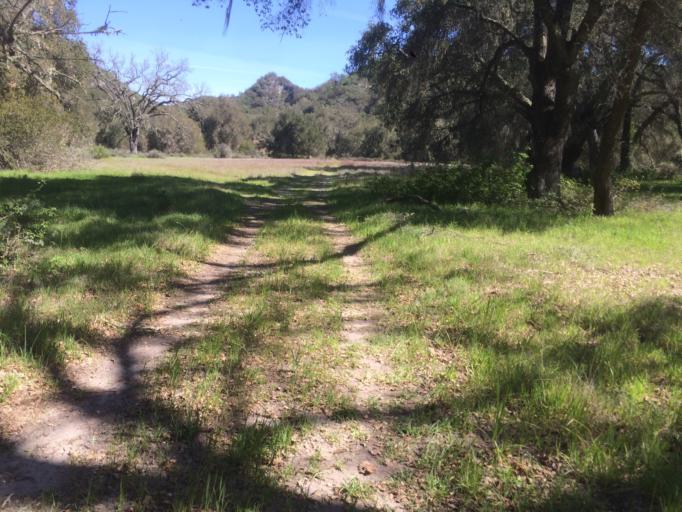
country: US
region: California
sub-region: San Luis Obispo County
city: Nipomo
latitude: 35.1782
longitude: -120.3926
